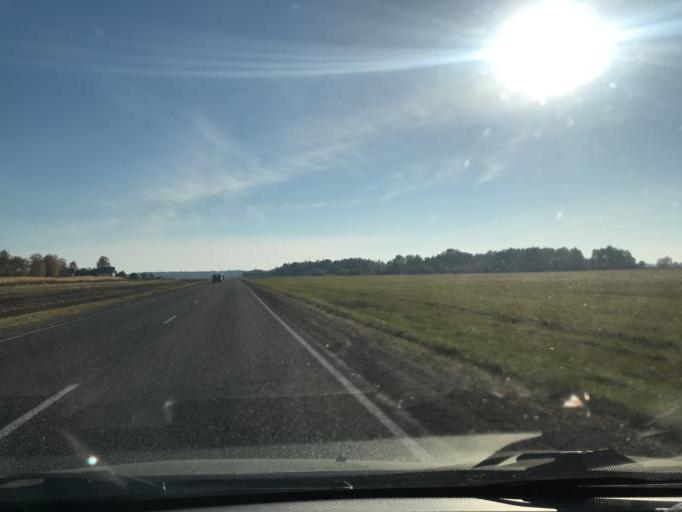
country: BY
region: Gomel
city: Brahin
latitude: 51.7743
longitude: 30.2640
